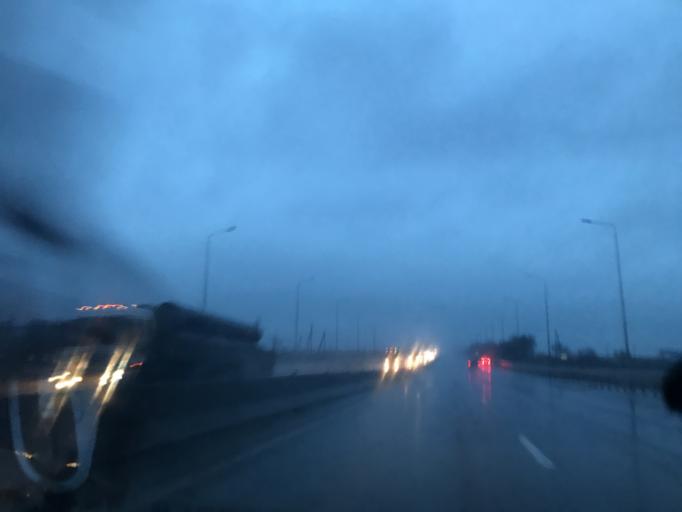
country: RU
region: Rostov
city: Samarskoye
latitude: 47.0017
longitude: 39.7305
